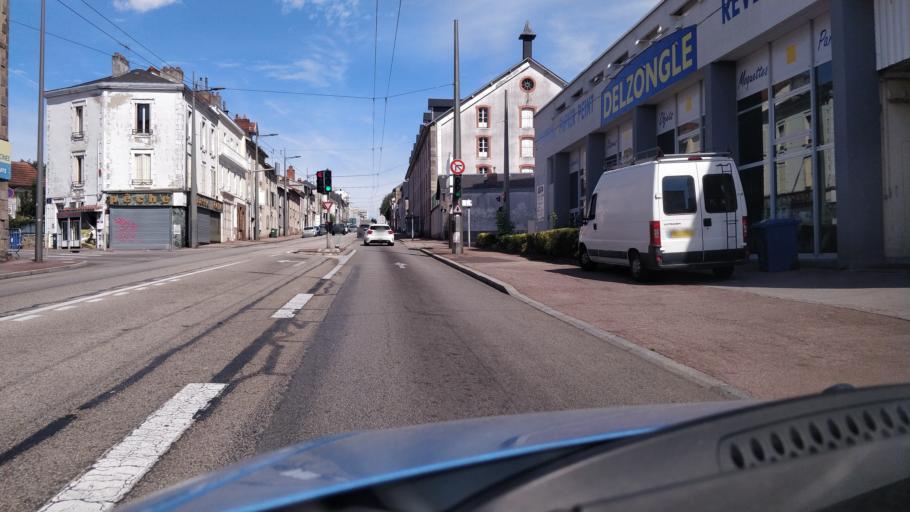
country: FR
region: Limousin
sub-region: Departement de la Haute-Vienne
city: Limoges
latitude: 45.8443
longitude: 1.2599
